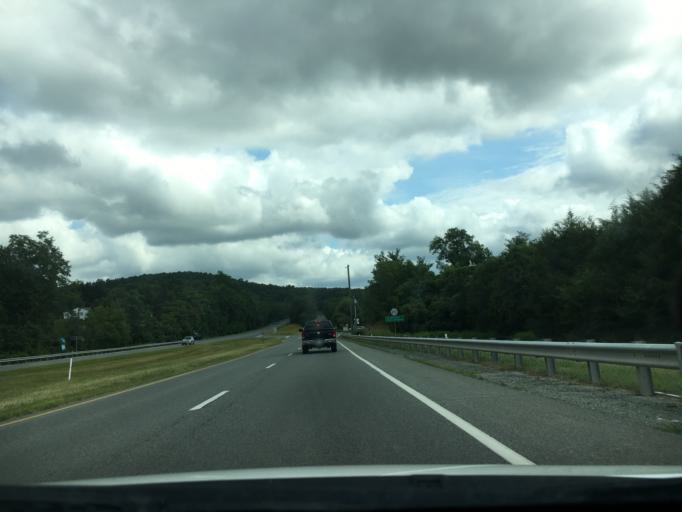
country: US
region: Virginia
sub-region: Albemarle County
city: Crozet
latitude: 37.9549
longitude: -78.6603
